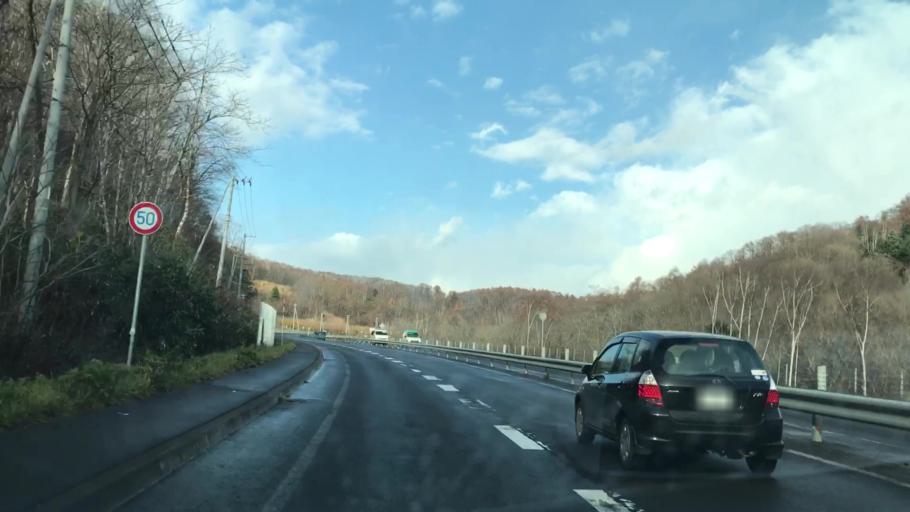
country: JP
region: Hokkaido
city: Yoichi
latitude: 43.2145
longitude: 140.7470
